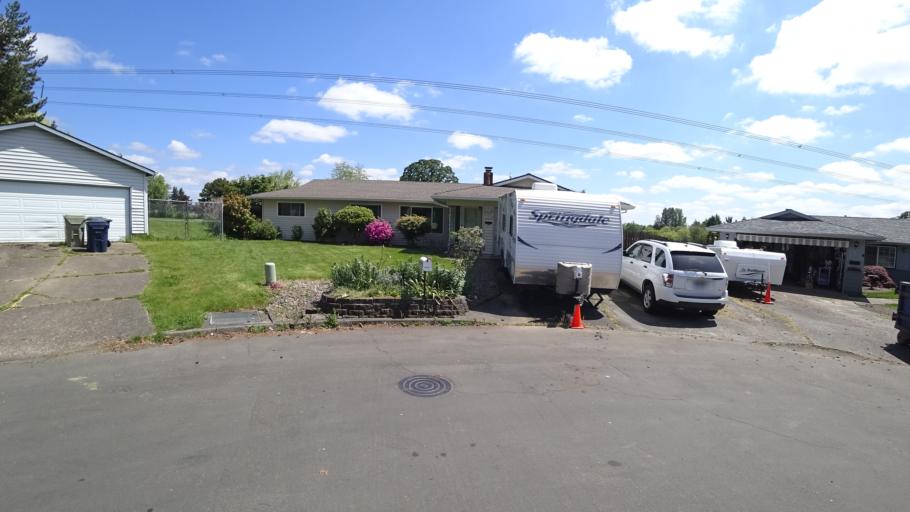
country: US
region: Oregon
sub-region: Washington County
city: Aloha
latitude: 45.5065
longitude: -122.8982
